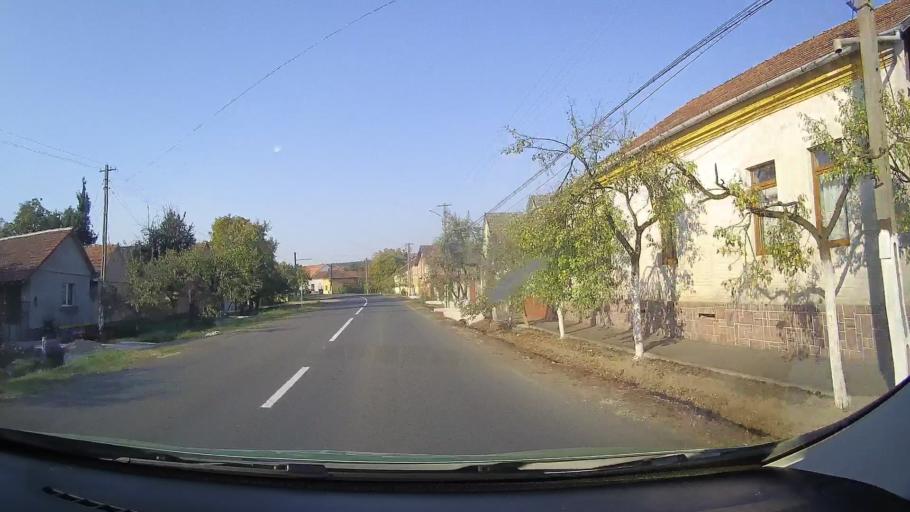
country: RO
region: Arad
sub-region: Comuna Ghioroc
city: Ghioroc
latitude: 46.1371
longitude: 21.6048
